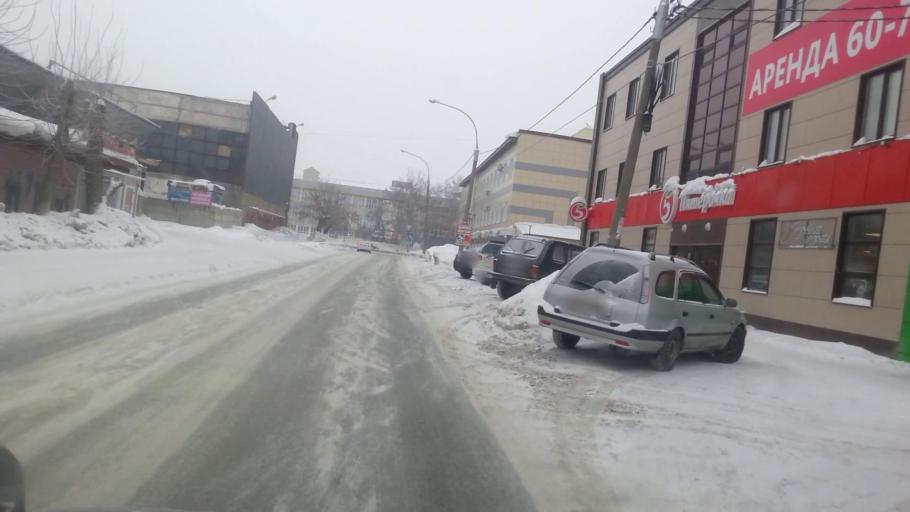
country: RU
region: Altai Krai
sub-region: Gorod Barnaulskiy
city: Barnaul
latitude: 53.3824
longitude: 83.7373
